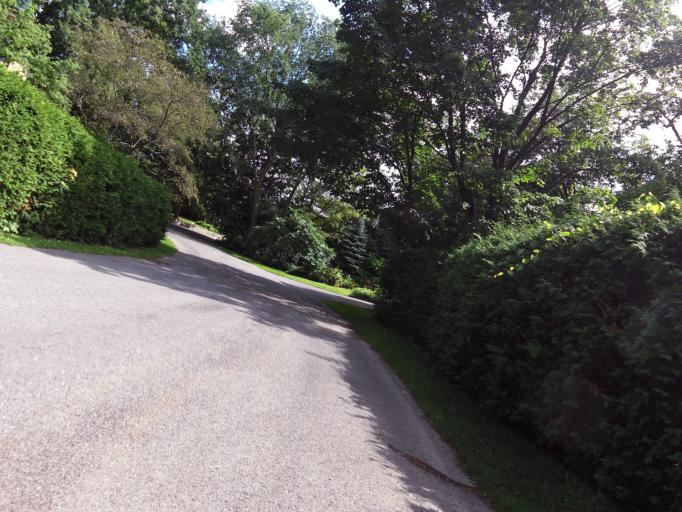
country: CA
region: Quebec
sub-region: Outaouais
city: Gatineau
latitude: 45.4461
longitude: -75.6704
